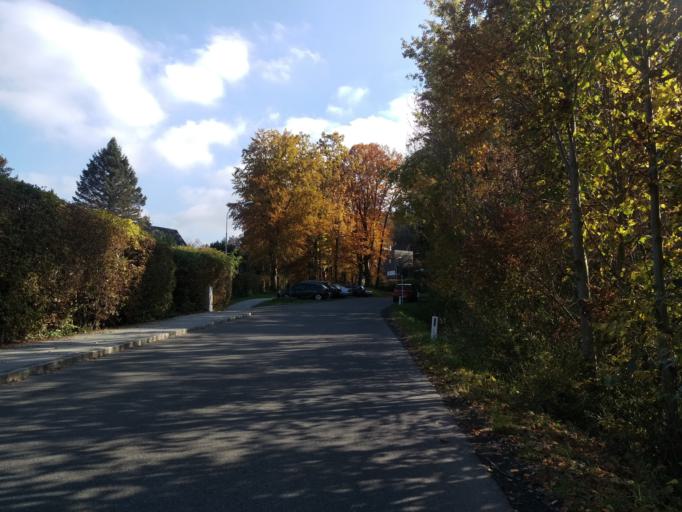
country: AT
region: Styria
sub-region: Graz Stadt
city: Mariatrost
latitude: 47.1056
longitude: 15.4952
